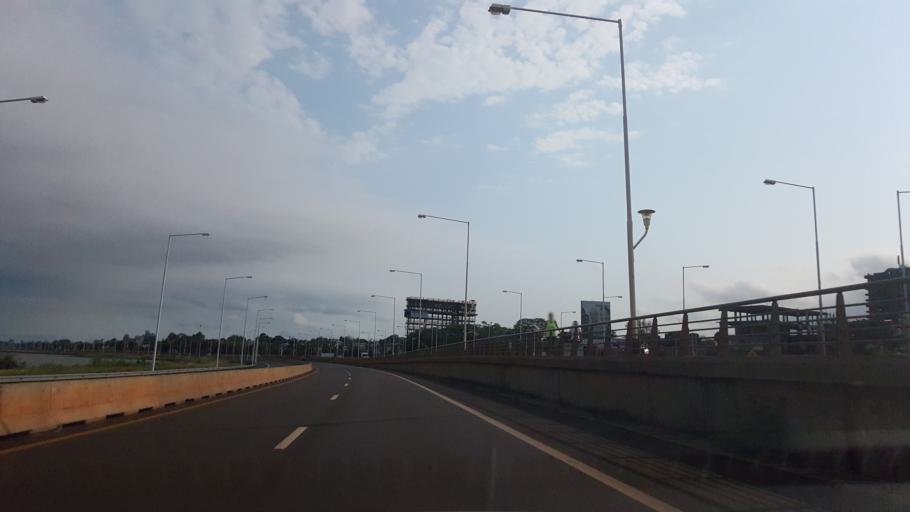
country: AR
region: Misiones
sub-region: Departamento de Capital
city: Posadas
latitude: -27.3907
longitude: -55.8910
